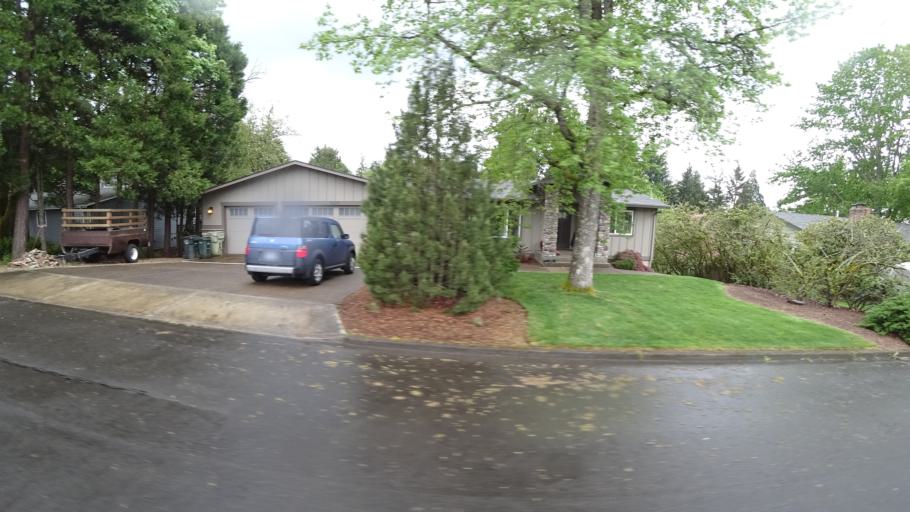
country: US
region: Oregon
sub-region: Washington County
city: West Haven
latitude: 45.5303
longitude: -122.7704
